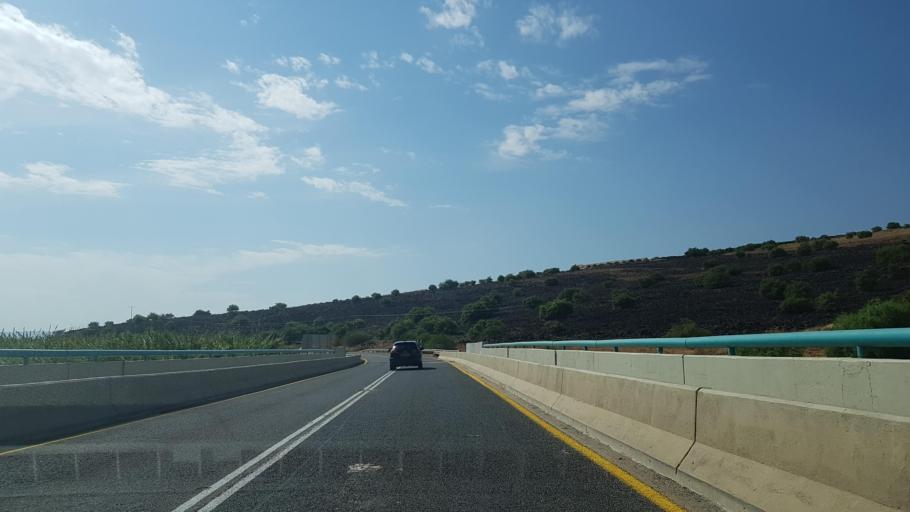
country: SY
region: Quneitra
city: Al Butayhah
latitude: 32.9015
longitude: 35.6136
